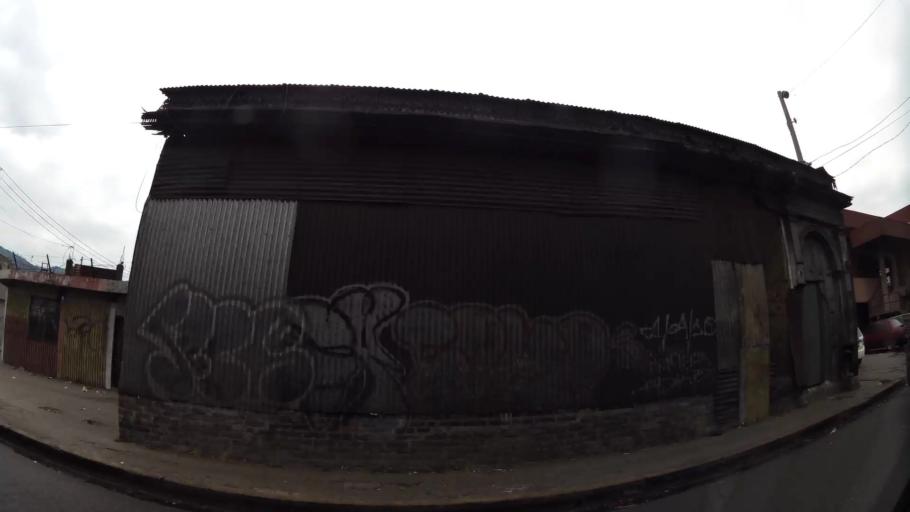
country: SV
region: San Salvador
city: San Salvador
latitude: 13.6993
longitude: -89.1857
